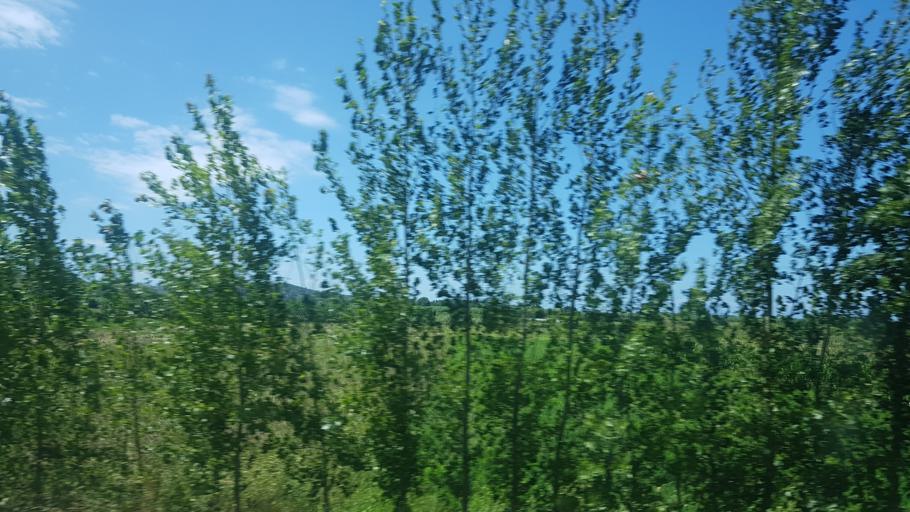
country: AL
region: Fier
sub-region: Rrethi i Fierit
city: Frakulla e Madhe
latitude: 40.6184
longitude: 19.5188
